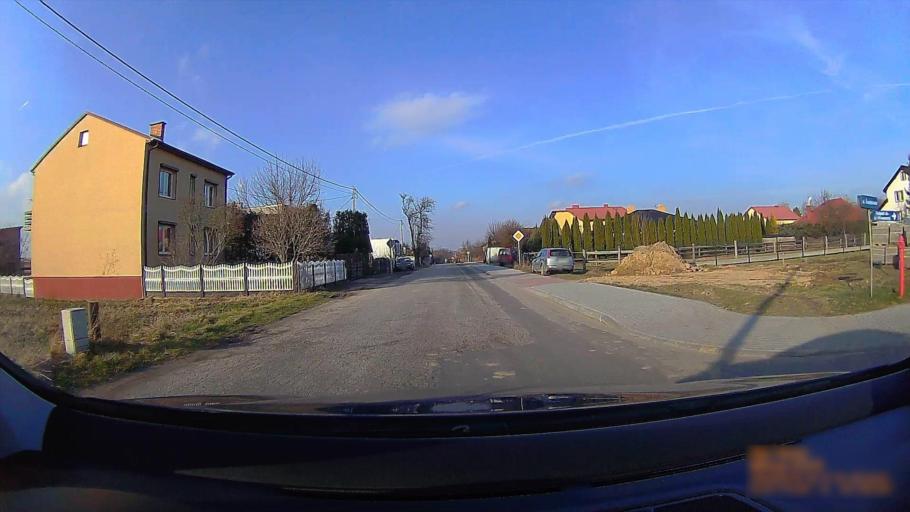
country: PL
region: Greater Poland Voivodeship
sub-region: Konin
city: Konin
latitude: 52.1842
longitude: 18.3014
